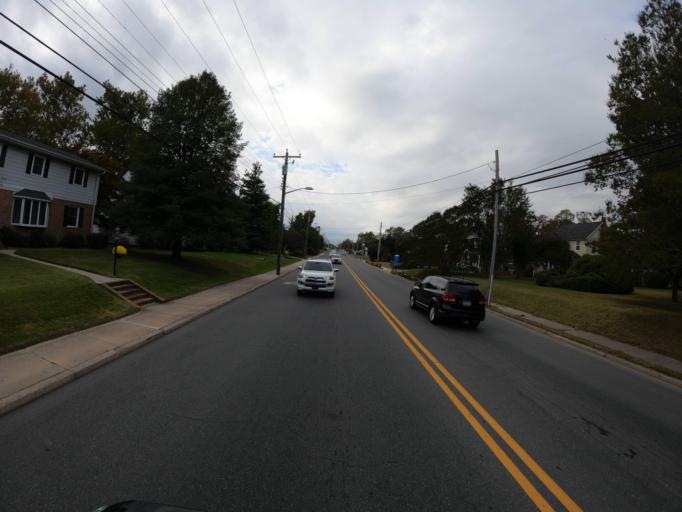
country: US
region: Delaware
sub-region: Sussex County
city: Lewes
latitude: 38.7673
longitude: -75.1467
